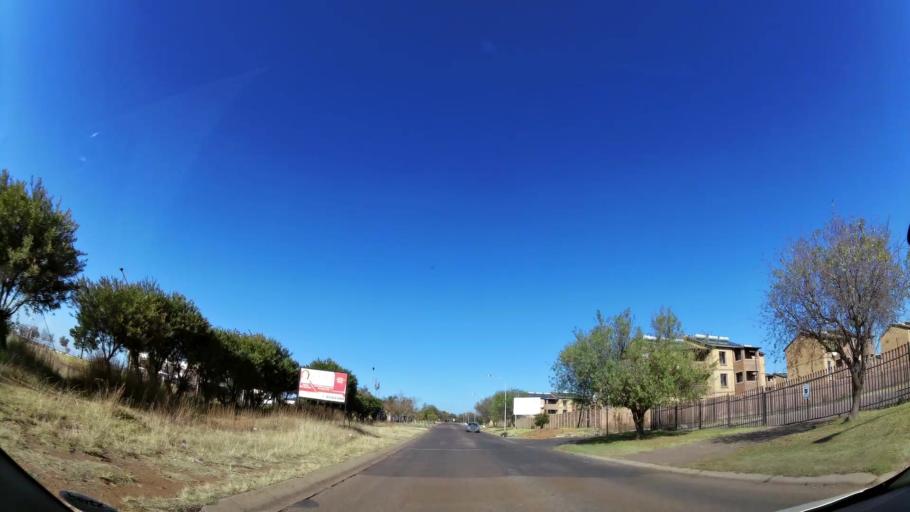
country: ZA
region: Mpumalanga
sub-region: Nkangala District Municipality
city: Witbank
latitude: -25.8829
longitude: 29.2564
